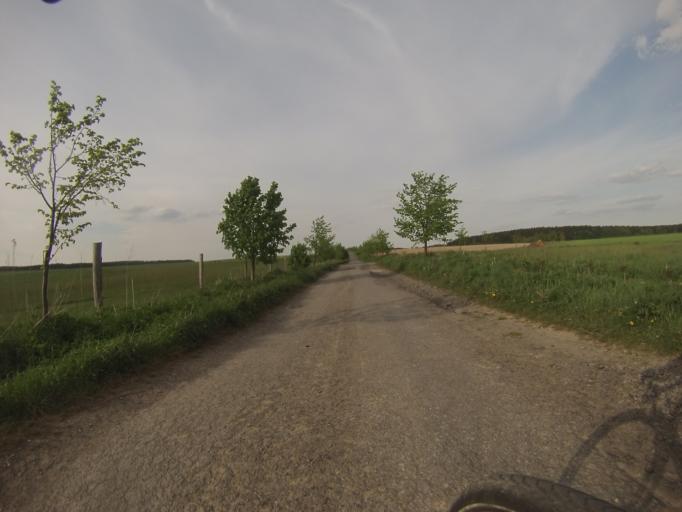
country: CZ
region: Olomoucky
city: Protivanov
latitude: 49.4458
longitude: 16.8608
